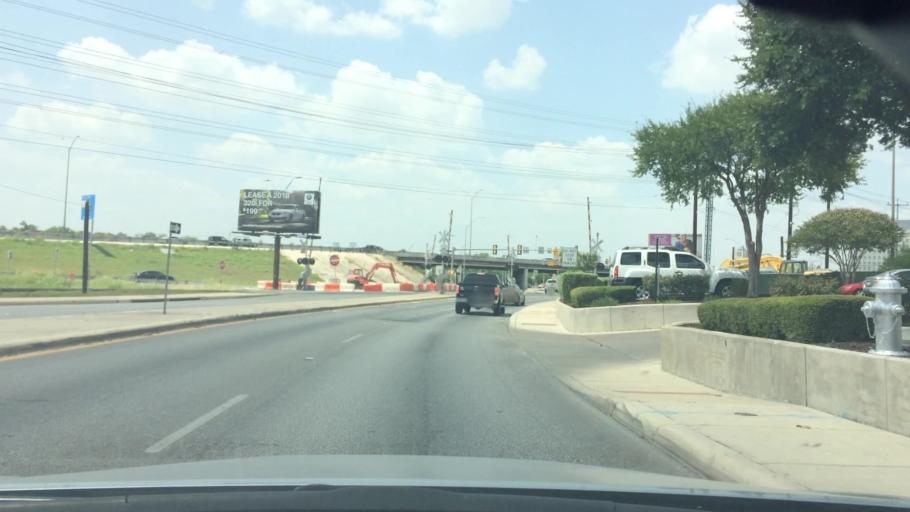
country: US
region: Texas
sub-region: Bexar County
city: Alamo Heights
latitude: 29.4988
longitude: -98.4814
